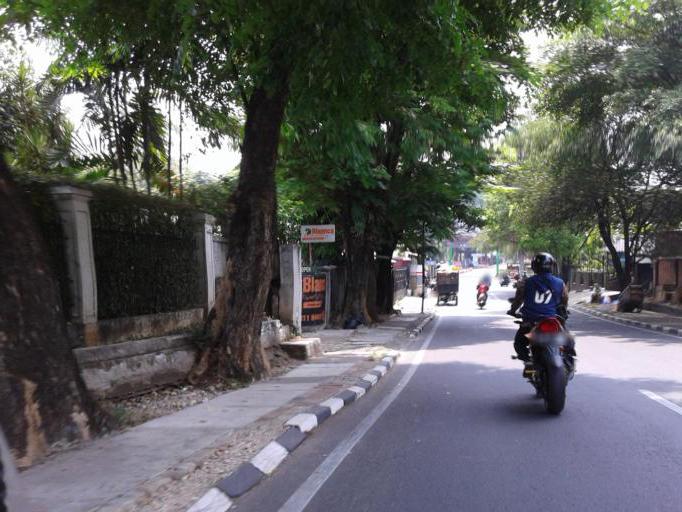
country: ID
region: West Java
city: Pamulang
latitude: -6.3108
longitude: 106.8155
